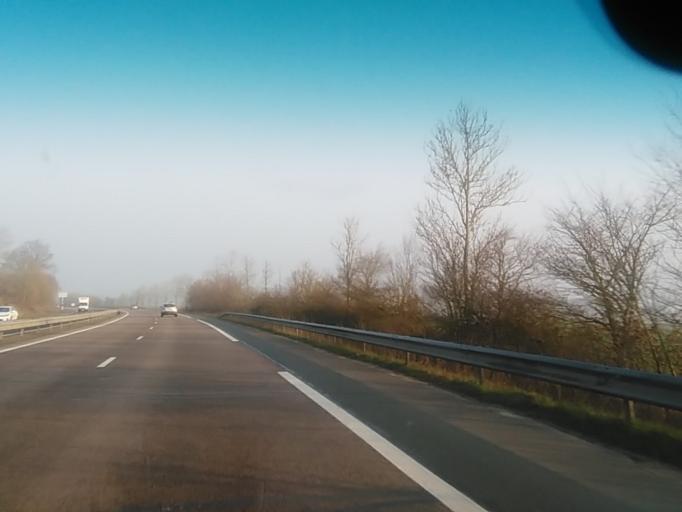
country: FR
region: Lower Normandy
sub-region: Departement du Calvados
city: Potigny
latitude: 48.9606
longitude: -0.2276
